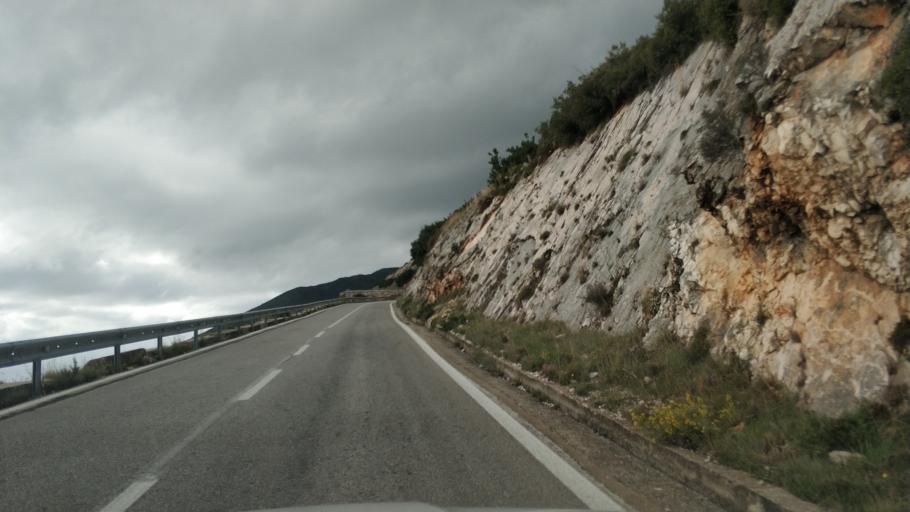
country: AL
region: Vlore
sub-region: Rrethi i Vlores
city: Vranisht
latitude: 40.1790
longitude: 19.5958
